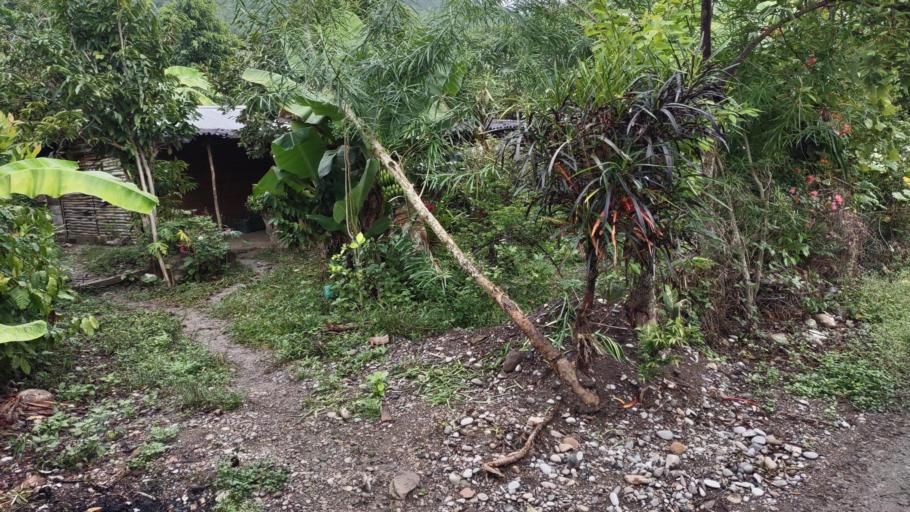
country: MX
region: Puebla
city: Espinal
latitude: 20.2629
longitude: -97.3684
